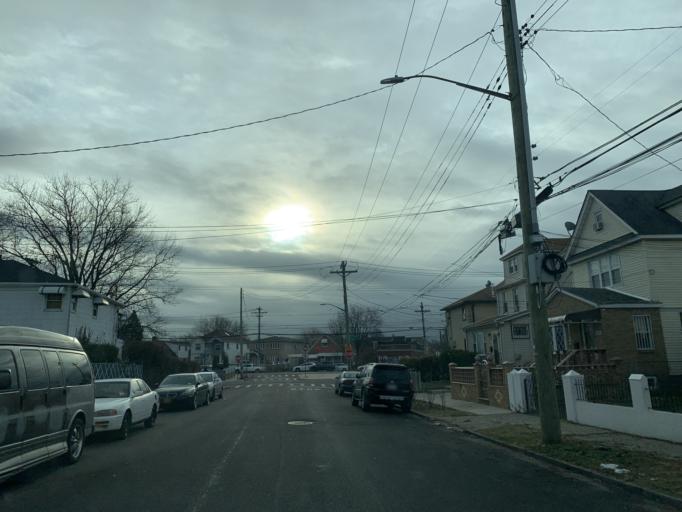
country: US
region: New York
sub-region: Queens County
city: Jamaica
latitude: 40.6869
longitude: -73.8021
